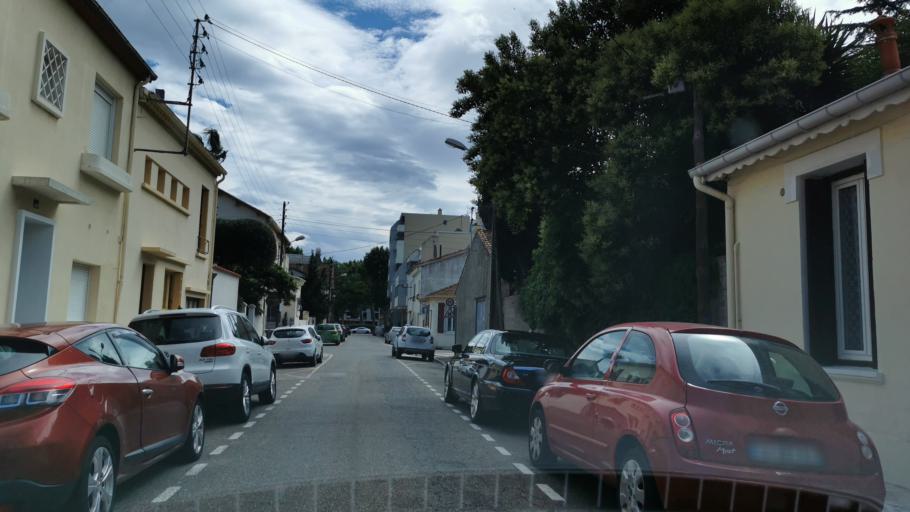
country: FR
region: Languedoc-Roussillon
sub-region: Departement de l'Aude
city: Narbonne
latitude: 43.1817
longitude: 3.0120
